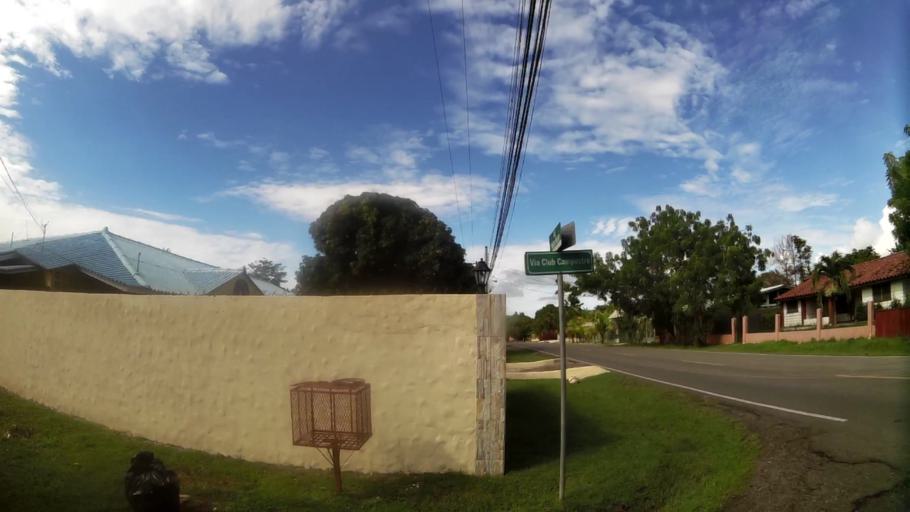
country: PA
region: Panama
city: Nueva Gorgona
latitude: 8.5318
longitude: -79.8883
